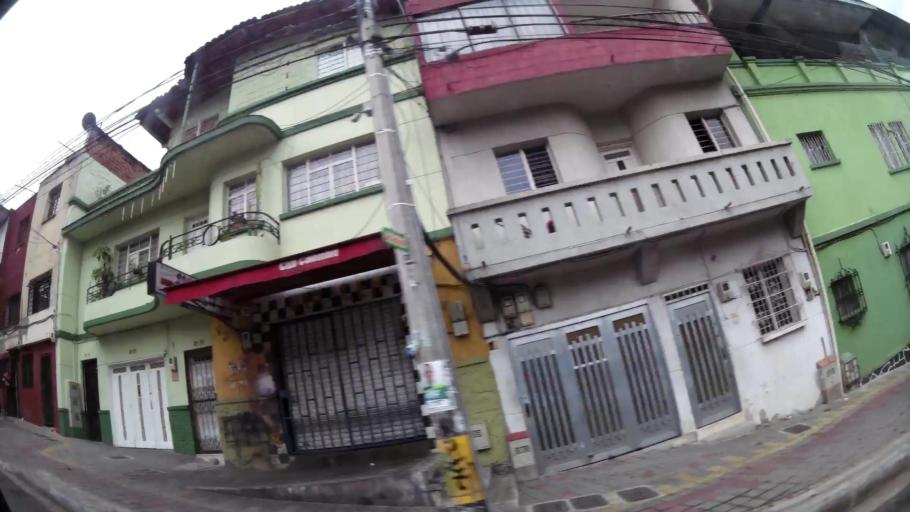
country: CO
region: Antioquia
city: Medellin
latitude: 6.2395
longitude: -75.5536
